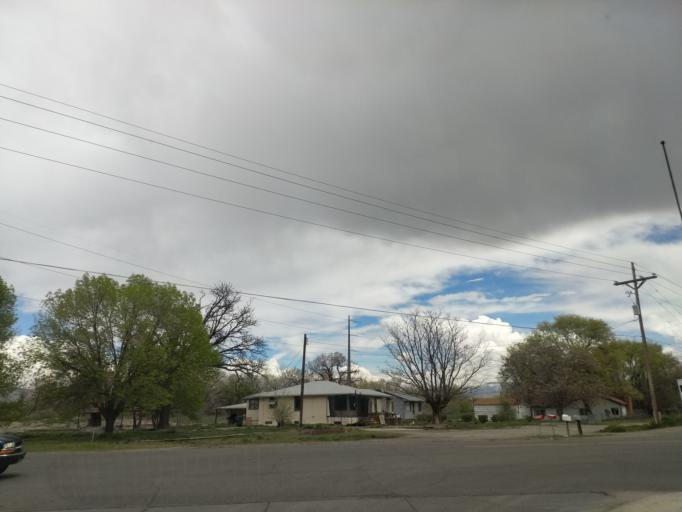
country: US
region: Colorado
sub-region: Mesa County
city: Grand Junction
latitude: 39.0667
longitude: -108.5865
